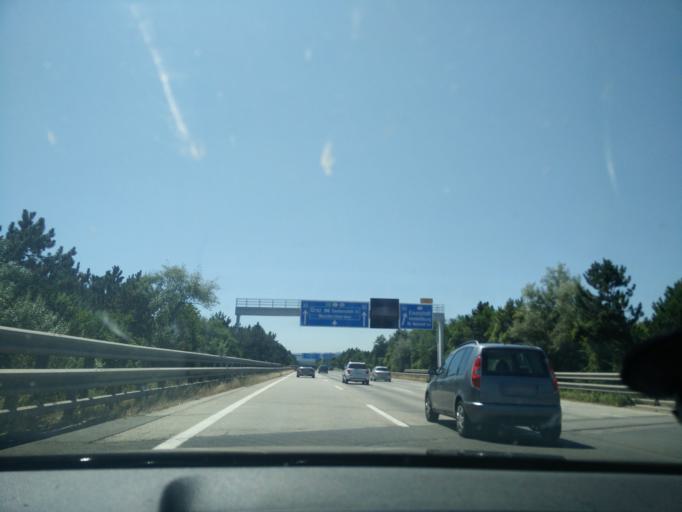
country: AT
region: Lower Austria
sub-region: Wiener Neustadt Stadt
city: Wiener Neustadt
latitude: 47.7864
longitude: 16.2040
